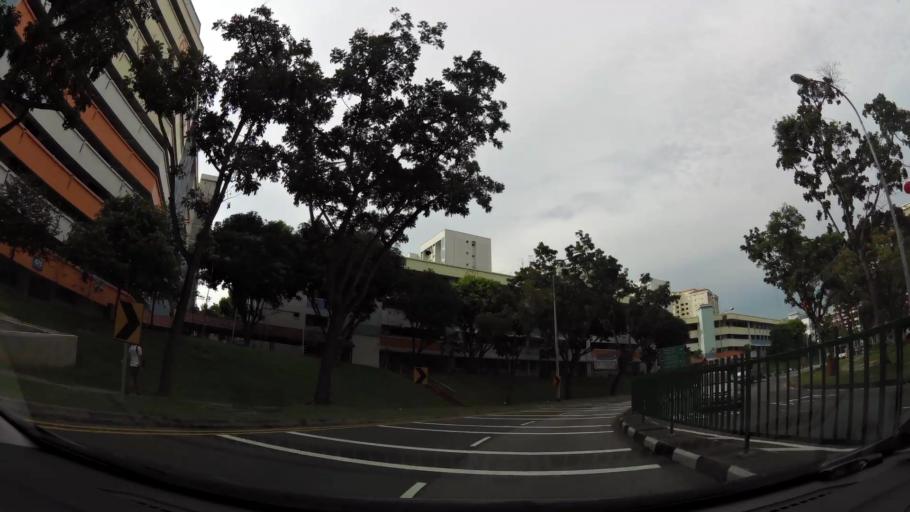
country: SG
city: Singapore
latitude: 1.3727
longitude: 103.8851
